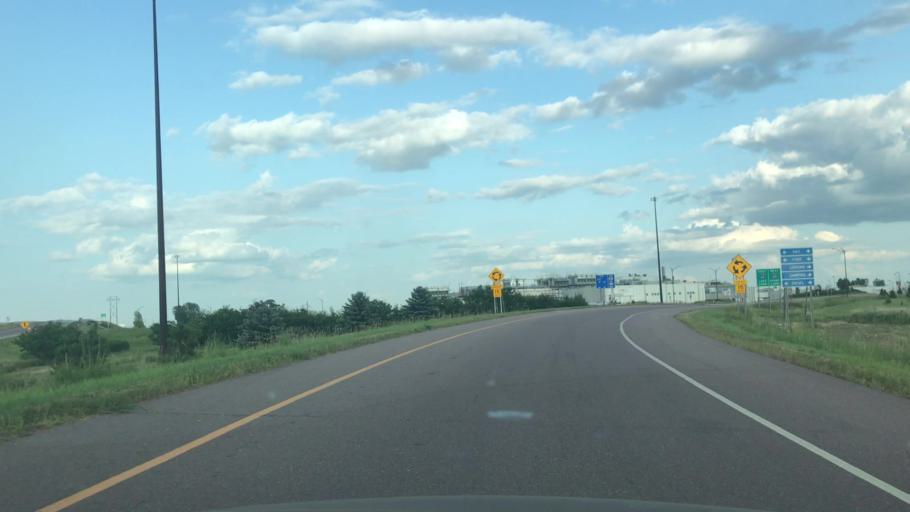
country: US
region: Minnesota
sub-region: Nobles County
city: Worthington
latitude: 43.6372
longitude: -95.5713
